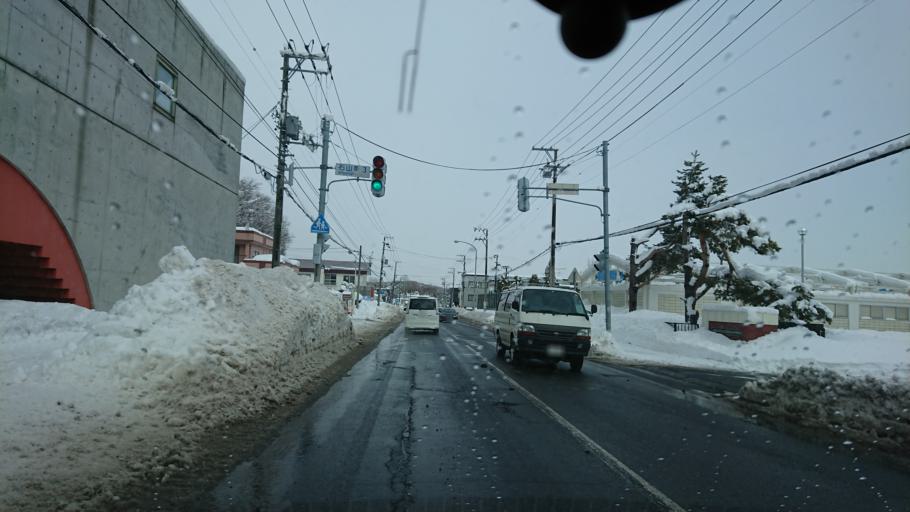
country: JP
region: Hokkaido
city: Sapporo
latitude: 42.9666
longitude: 141.3427
